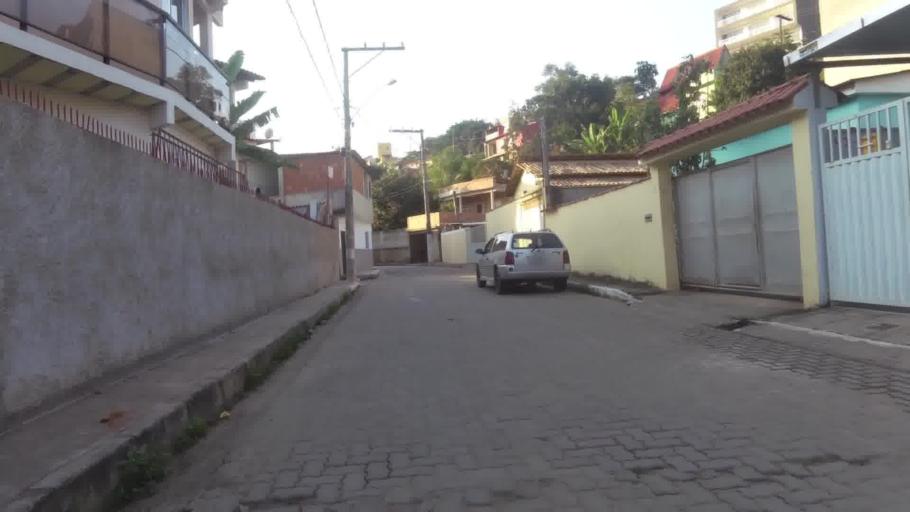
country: BR
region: Espirito Santo
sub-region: Piuma
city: Piuma
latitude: -20.8340
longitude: -40.7215
